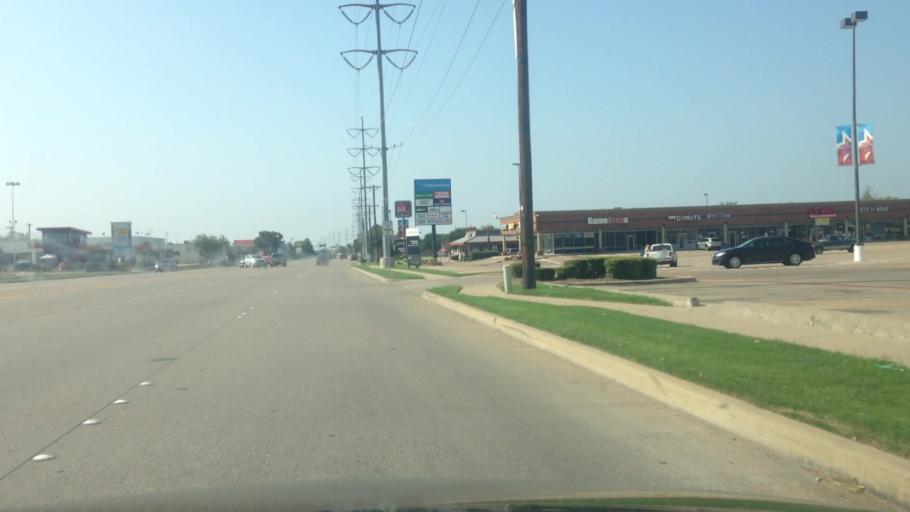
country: US
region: Texas
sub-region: Tarrant County
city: Watauga
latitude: 32.8597
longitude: -97.2382
